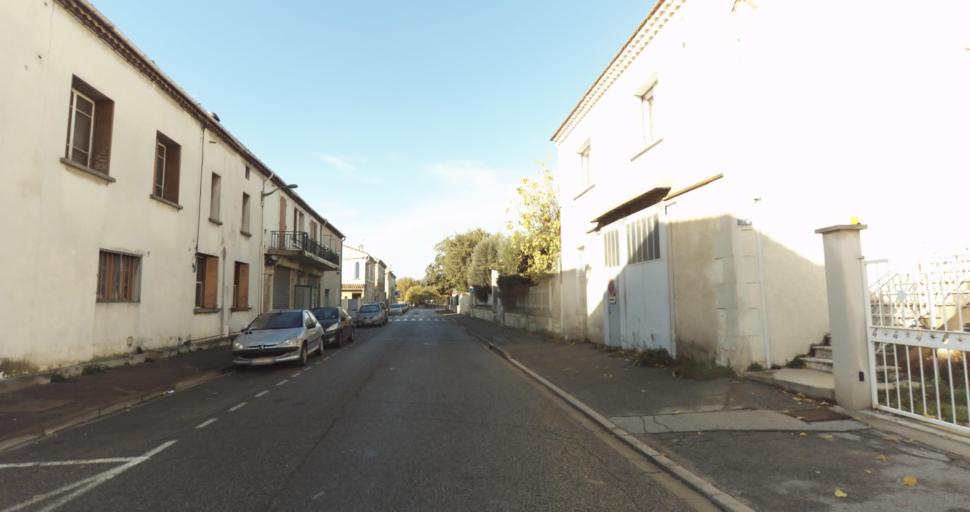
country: FR
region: Provence-Alpes-Cote d'Azur
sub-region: Departement des Bouches-du-Rhone
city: Rognonas
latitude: 43.8982
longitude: 4.8007
